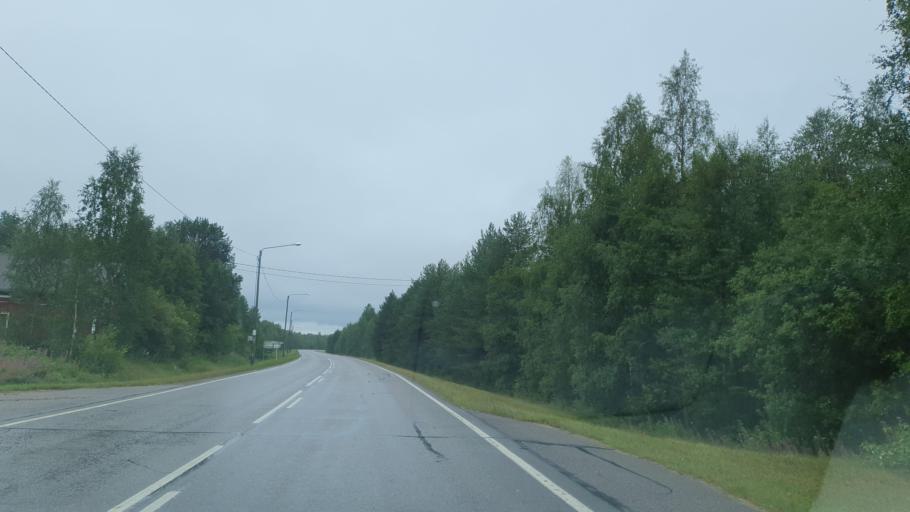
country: FI
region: Lapland
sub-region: Itae-Lappi
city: Kemijaervi
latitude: 66.6962
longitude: 27.5841
